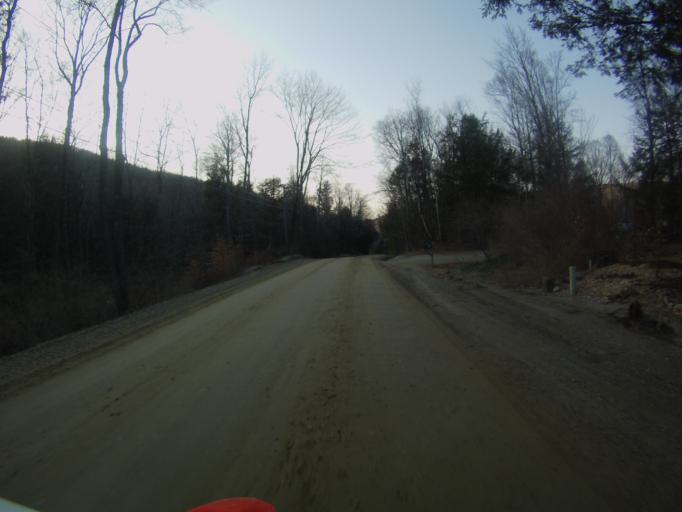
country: US
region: Vermont
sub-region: Addison County
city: Bristol
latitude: 44.0708
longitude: -73.0580
